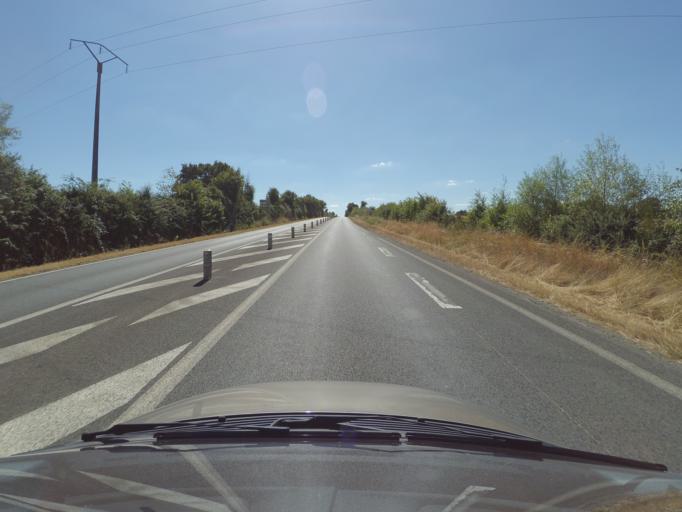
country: FR
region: Pays de la Loire
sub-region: Departement de Maine-et-Loire
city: Vezins
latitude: 47.1120
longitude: -0.7360
